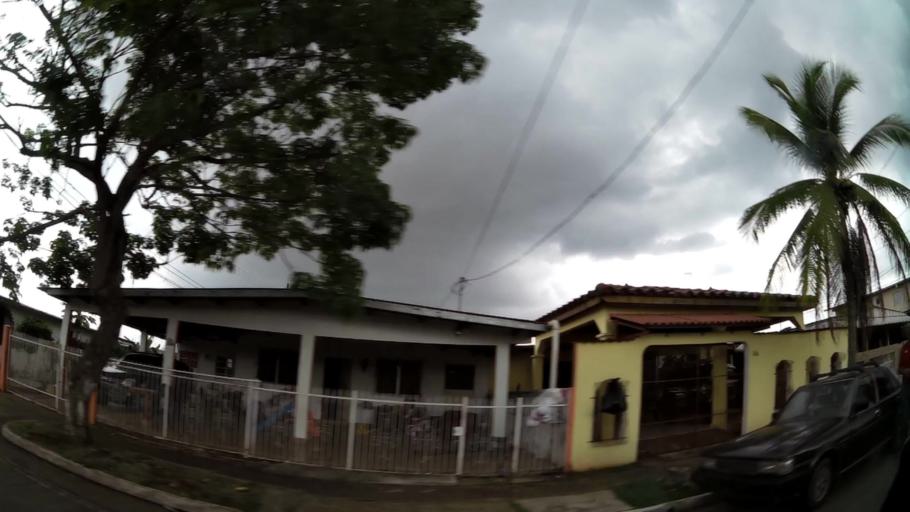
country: PA
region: Panama
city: Tocumen
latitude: 9.0577
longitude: -79.4167
